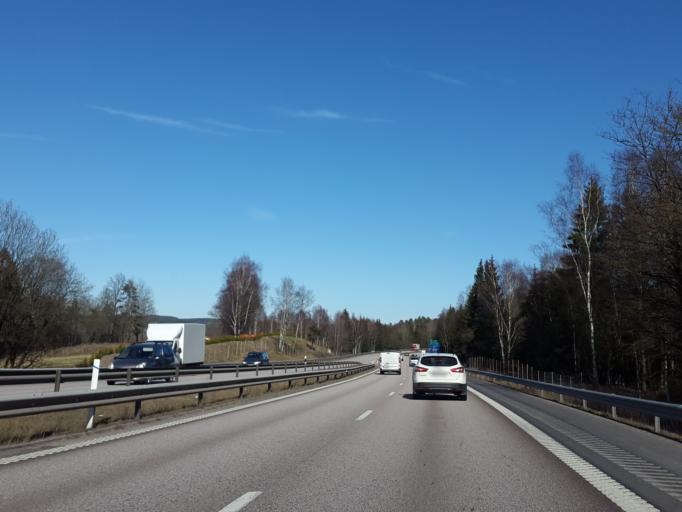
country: SE
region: Vaestra Goetaland
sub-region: Lerums Kommun
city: Lerum
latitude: 57.7442
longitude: 12.2216
